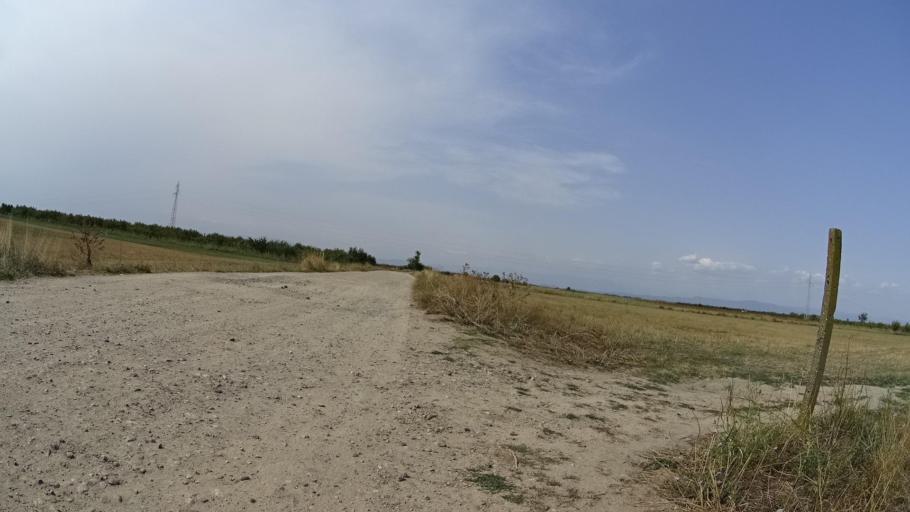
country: BG
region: Plovdiv
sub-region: Obshtina Kaloyanovo
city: Kaloyanovo
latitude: 42.2719
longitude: 24.8016
